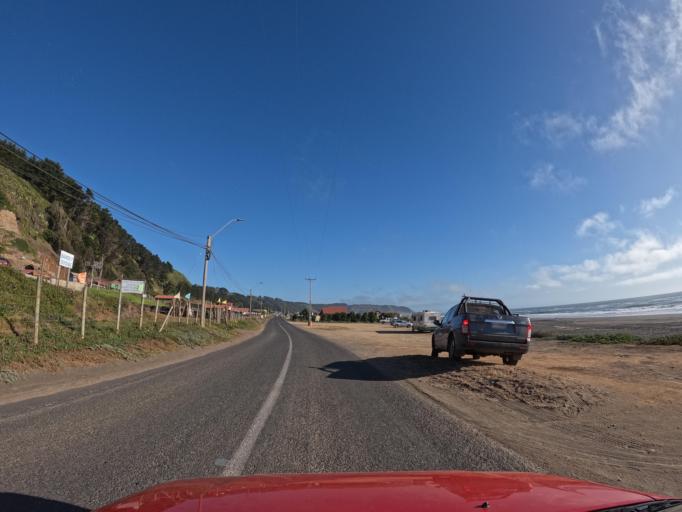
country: CL
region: Maule
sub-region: Provincia de Talca
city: Constitucion
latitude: -34.9171
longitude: -72.1818
